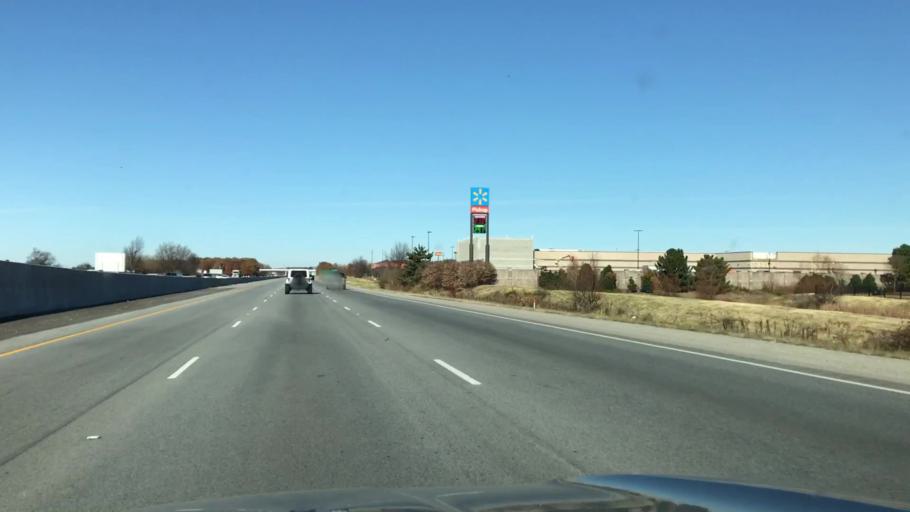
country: US
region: Arkansas
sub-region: Benton County
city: Lowell
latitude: 36.2765
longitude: -94.1513
